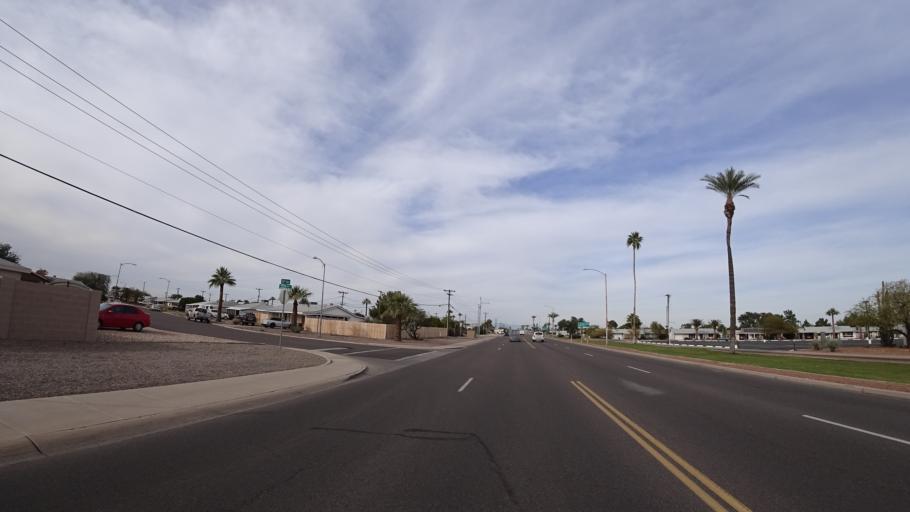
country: US
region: Arizona
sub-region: Maricopa County
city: Youngtown
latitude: 33.5843
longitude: -112.2988
